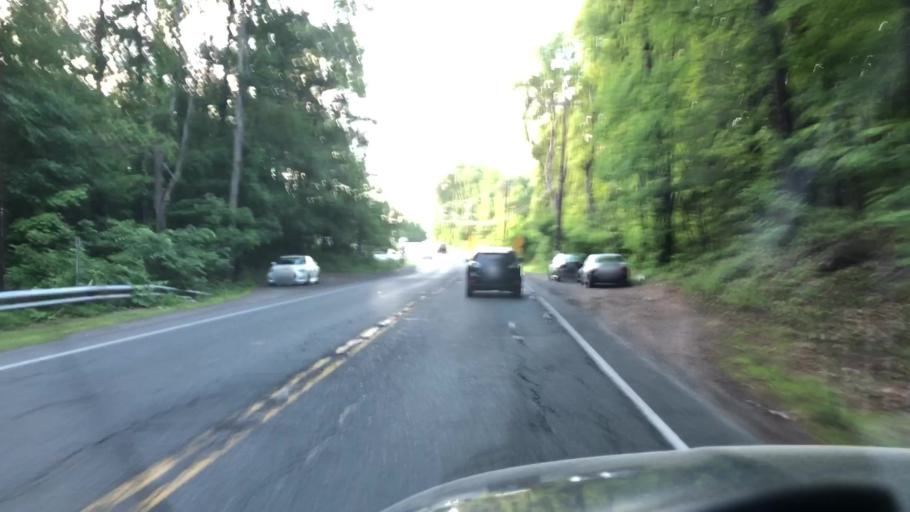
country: US
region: Massachusetts
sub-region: Hampshire County
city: Easthampton
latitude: 42.2351
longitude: -72.6506
